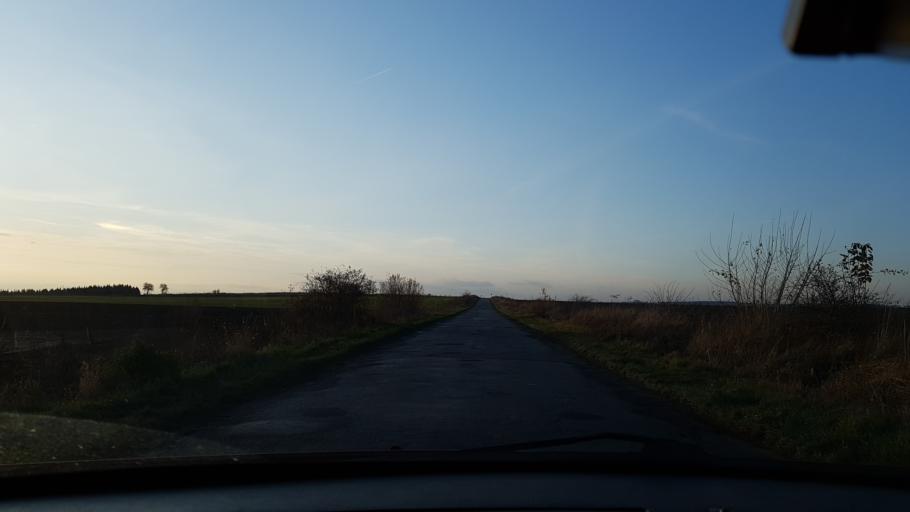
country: PL
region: Lower Silesian Voivodeship
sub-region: Powiat zabkowicki
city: Cieplowody
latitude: 50.6712
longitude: 16.9546
